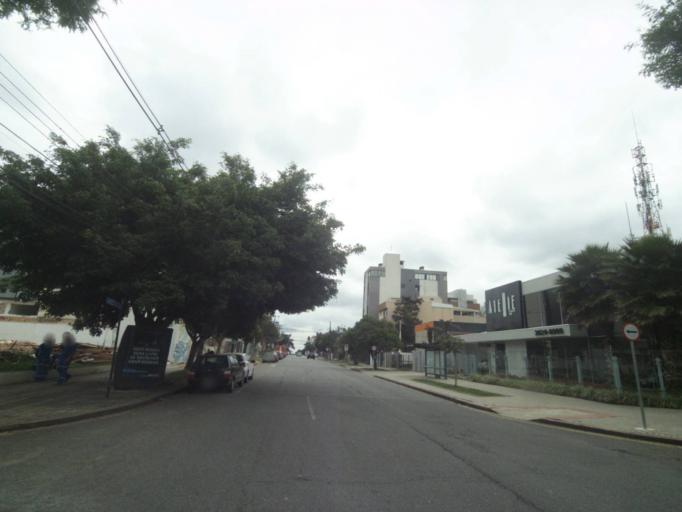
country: BR
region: Parana
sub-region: Curitiba
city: Curitiba
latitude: -25.4331
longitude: -49.2932
